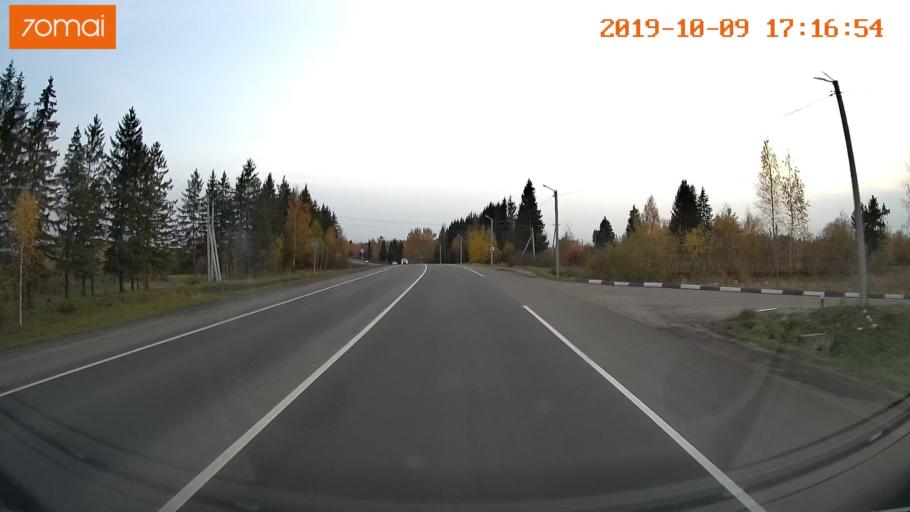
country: RU
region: Ivanovo
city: Furmanov
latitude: 57.2830
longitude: 41.1600
